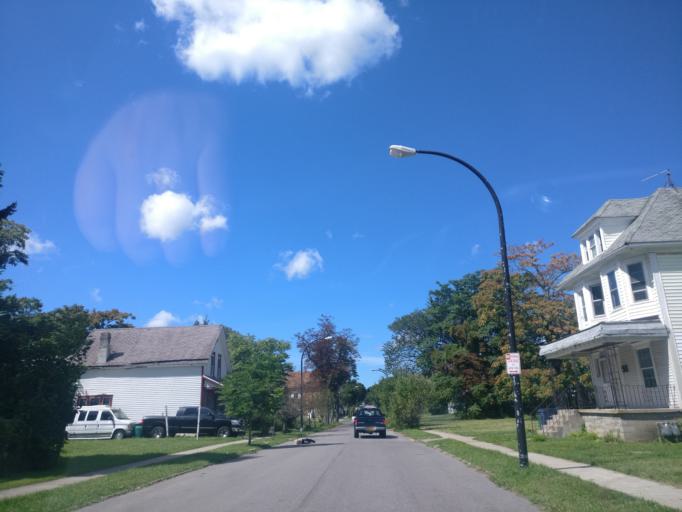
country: US
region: New York
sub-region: Erie County
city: Buffalo
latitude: 42.9102
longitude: -78.8610
